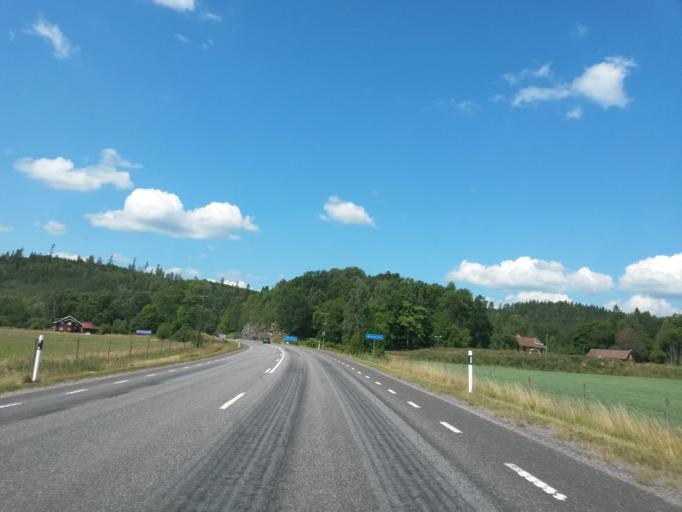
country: SE
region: Vaestra Goetaland
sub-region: Alingsas Kommun
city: Alingsas
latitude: 57.9742
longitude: 12.4402
